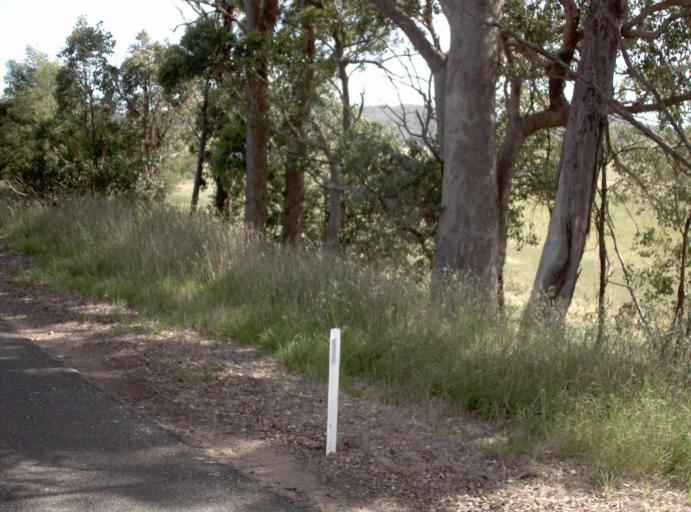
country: AU
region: Victoria
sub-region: East Gippsland
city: Lakes Entrance
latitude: -37.4922
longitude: 148.1308
